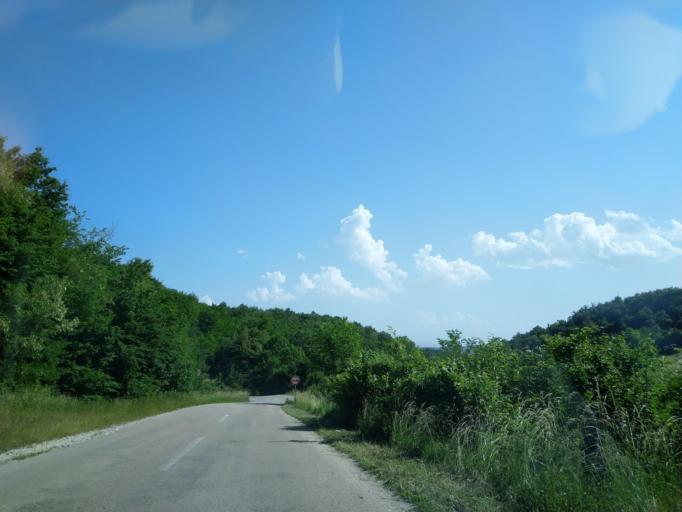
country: RS
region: Central Serbia
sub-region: Zlatiborski Okrug
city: Cajetina
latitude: 43.8676
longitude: 19.7139
